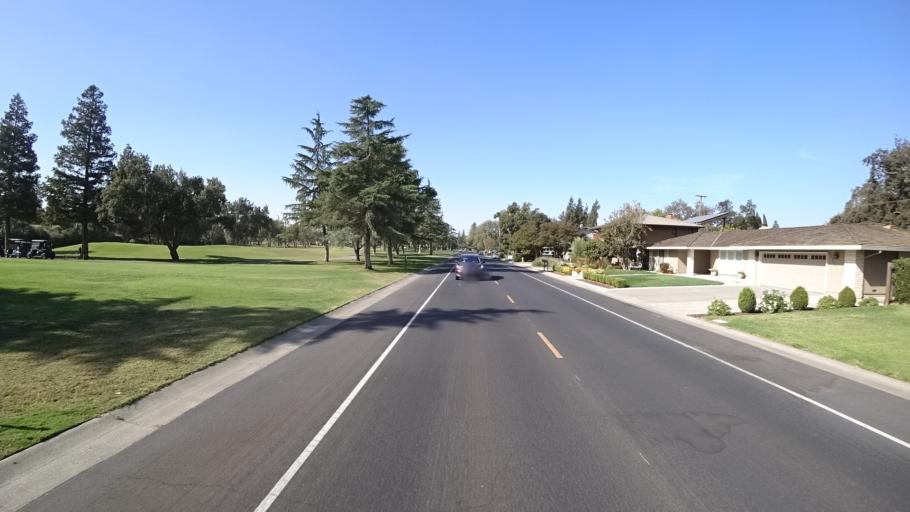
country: US
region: California
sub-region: Yolo County
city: Davis
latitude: 38.5479
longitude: -121.6893
